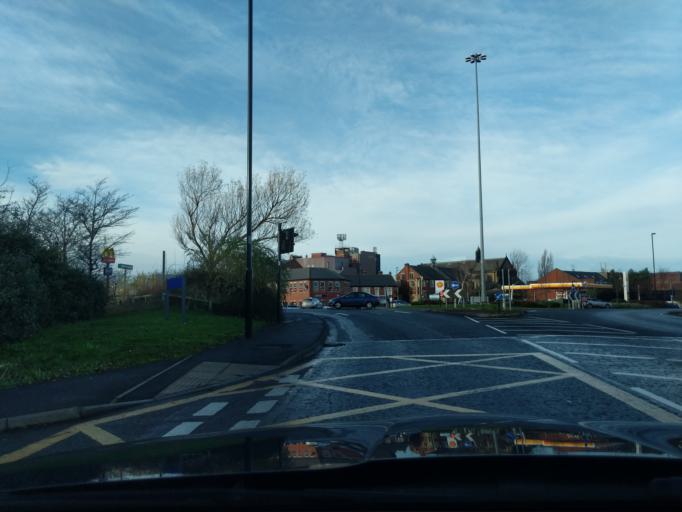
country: GB
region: England
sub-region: Gateshead
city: Felling
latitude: 54.9774
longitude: -1.5734
